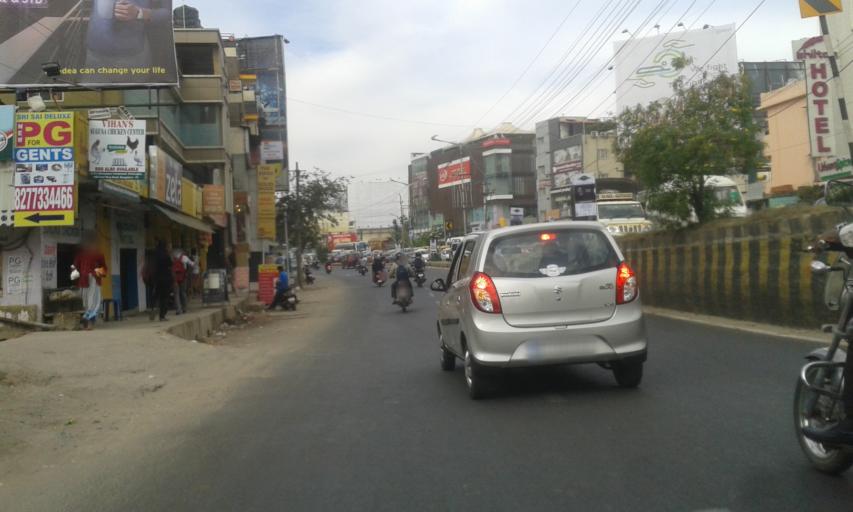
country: IN
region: Karnataka
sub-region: Bangalore Urban
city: Bangalore
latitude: 12.9384
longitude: 77.6303
